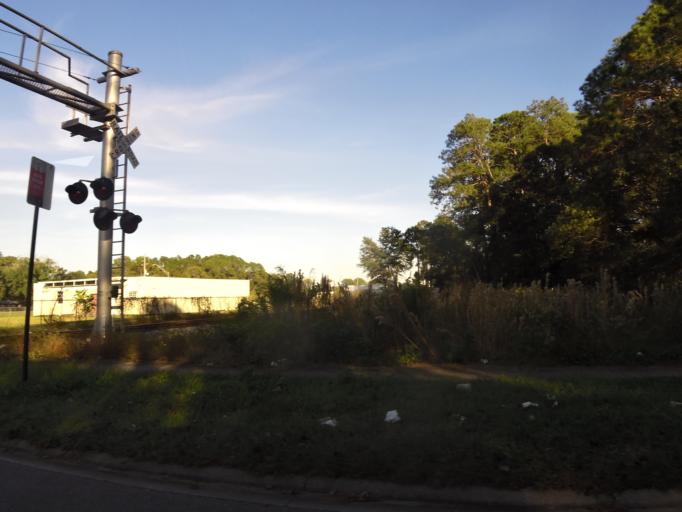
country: US
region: Florida
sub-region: Duval County
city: Jacksonville
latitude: 30.3559
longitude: -81.7013
